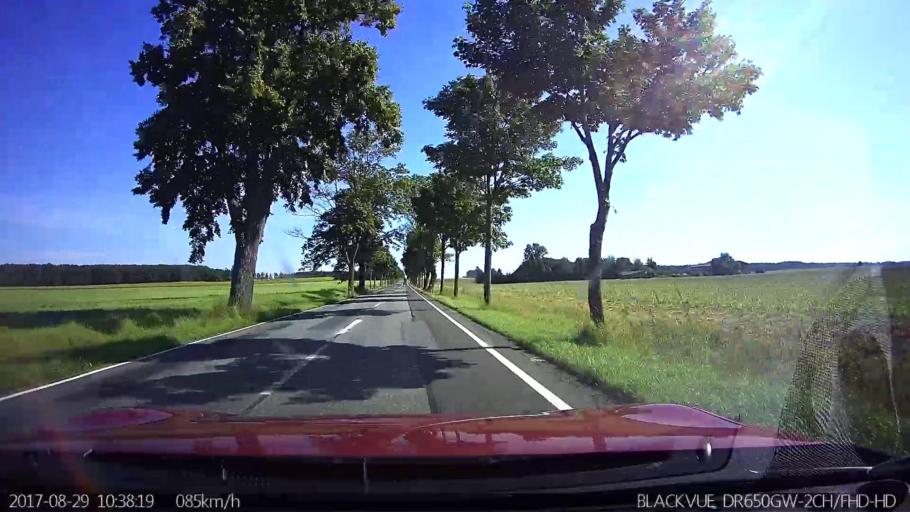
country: DE
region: Mecklenburg-Vorpommern
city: Franzburg
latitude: 54.1652
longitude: 12.8141
